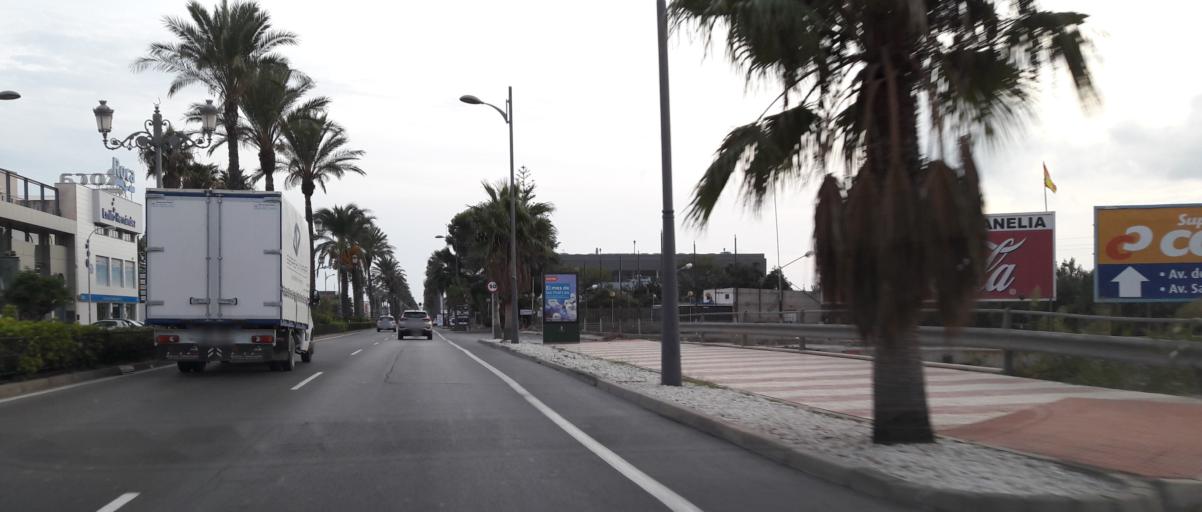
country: ES
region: Andalusia
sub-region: Provincia de Almeria
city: Roquetas de Mar
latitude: 36.7834
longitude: -2.6080
